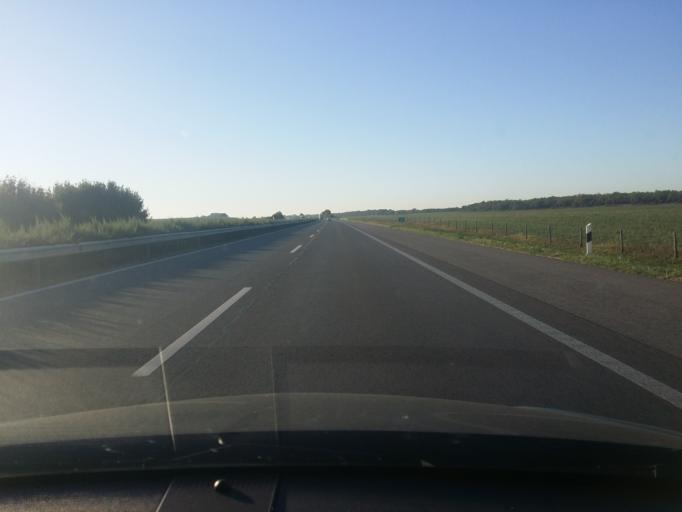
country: HU
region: Bacs-Kiskun
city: Varosfoeld
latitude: 46.8027
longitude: 19.7303
